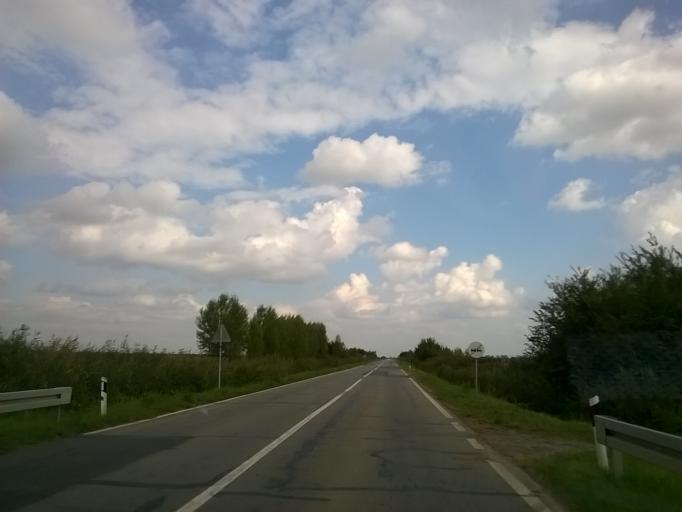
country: RS
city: Margita
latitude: 45.2251
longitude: 21.1500
